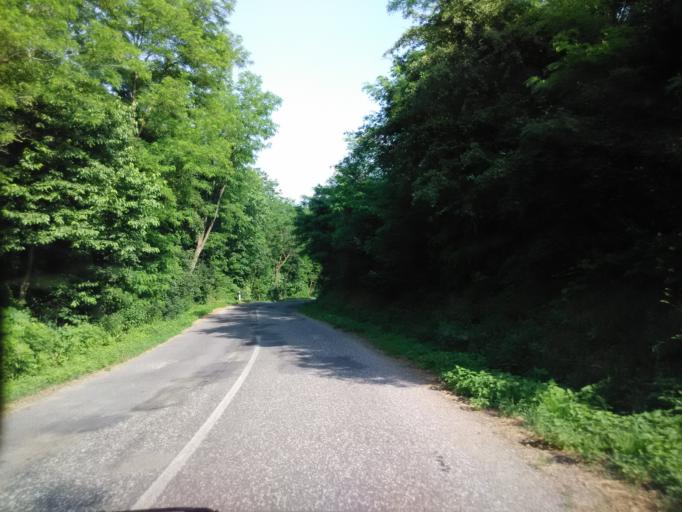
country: SK
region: Nitriansky
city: Levice
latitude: 48.2464
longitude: 18.6858
